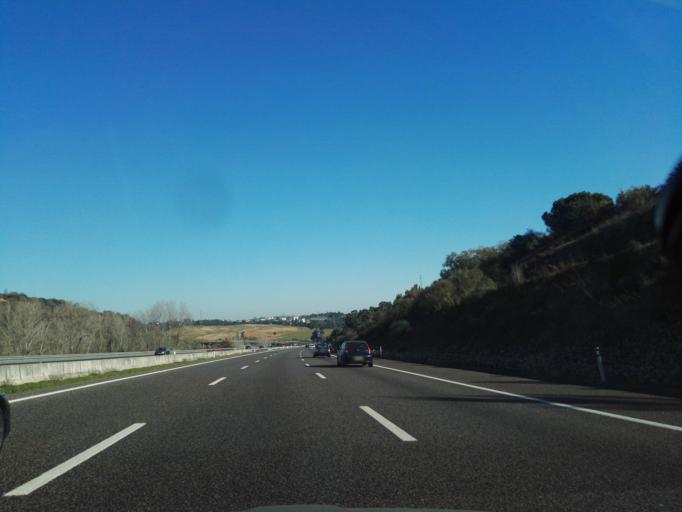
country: PT
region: Santarem
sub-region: Santarem
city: Santarem
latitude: 39.2388
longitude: -8.7560
